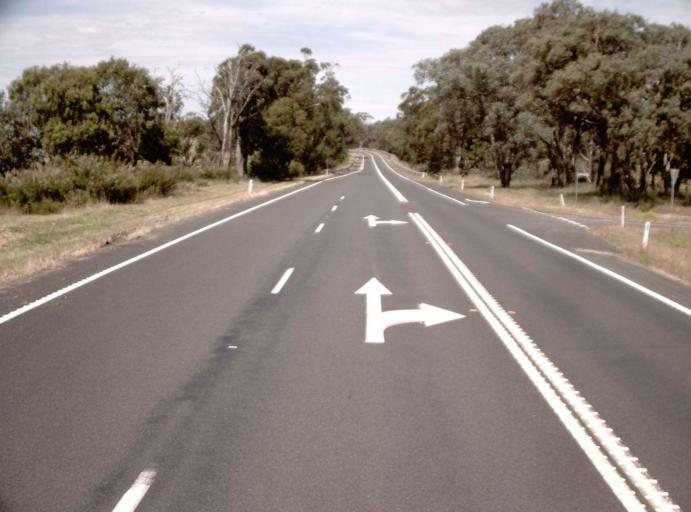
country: AU
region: Victoria
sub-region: Wellington
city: Sale
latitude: -37.9296
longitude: 147.2027
